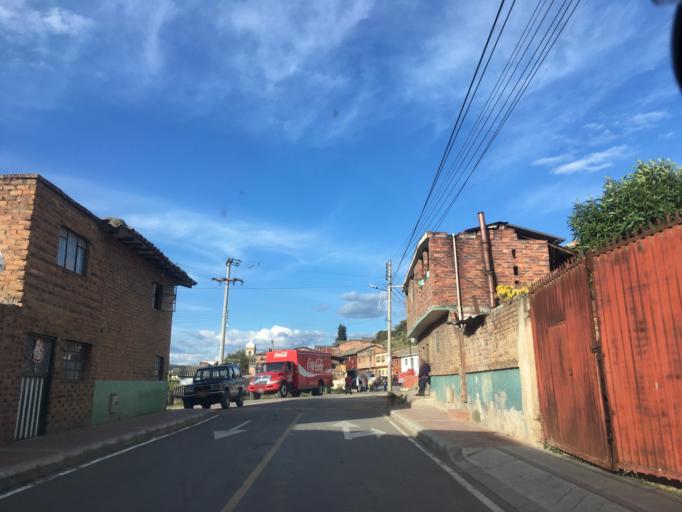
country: CO
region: Boyaca
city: Pesca
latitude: 5.5544
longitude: -73.0529
